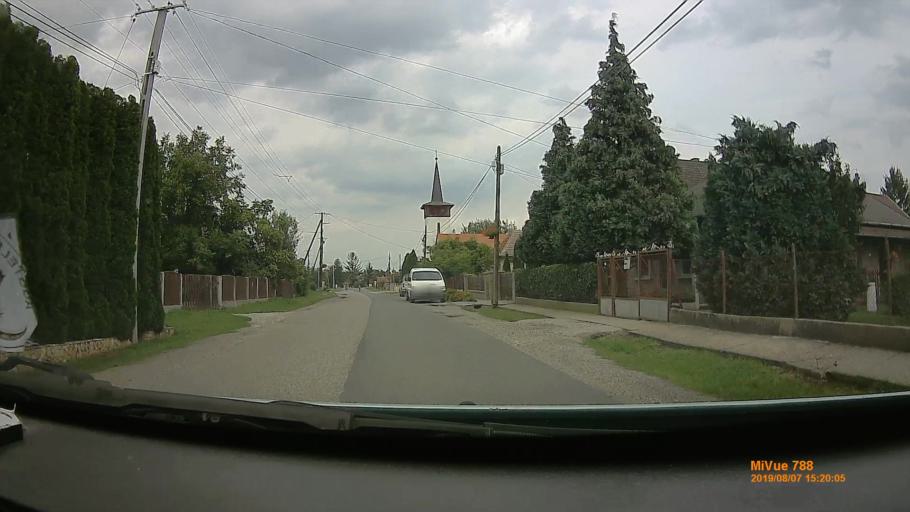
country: HU
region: Borsod-Abauj-Zemplen
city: Encs
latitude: 48.3537
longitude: 21.1458
